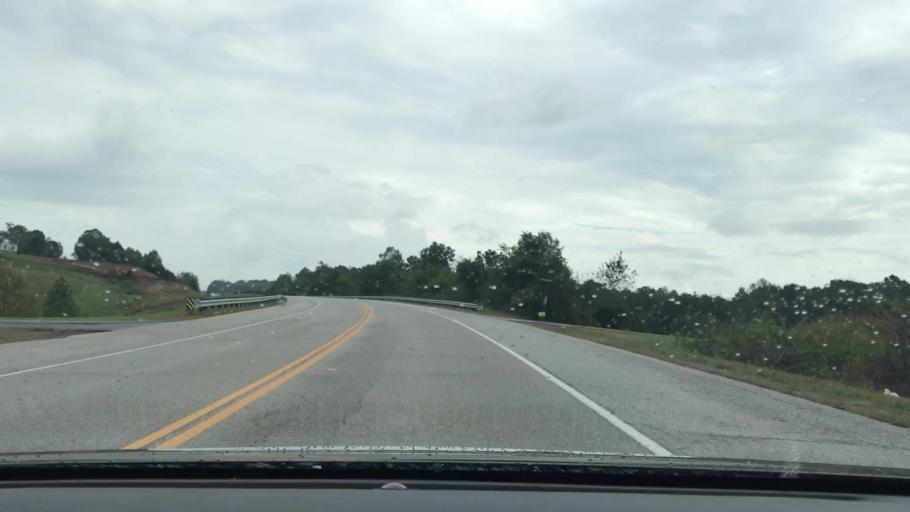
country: US
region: Tennessee
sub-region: Macon County
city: Red Boiling Springs
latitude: 36.5256
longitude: -85.8304
